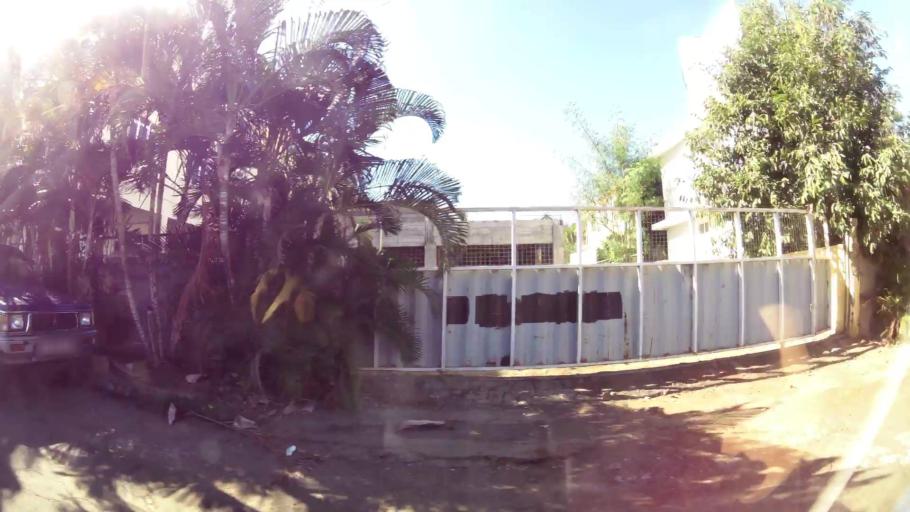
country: MU
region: Black River
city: Flic en Flac
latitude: -20.2770
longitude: 57.3758
